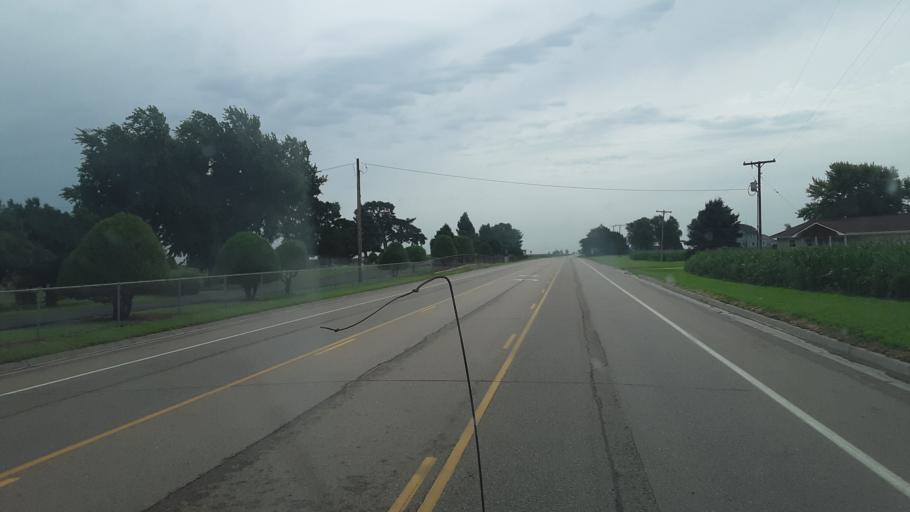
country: US
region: Kansas
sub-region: Stafford County
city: Saint John
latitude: 37.9565
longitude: -98.9594
